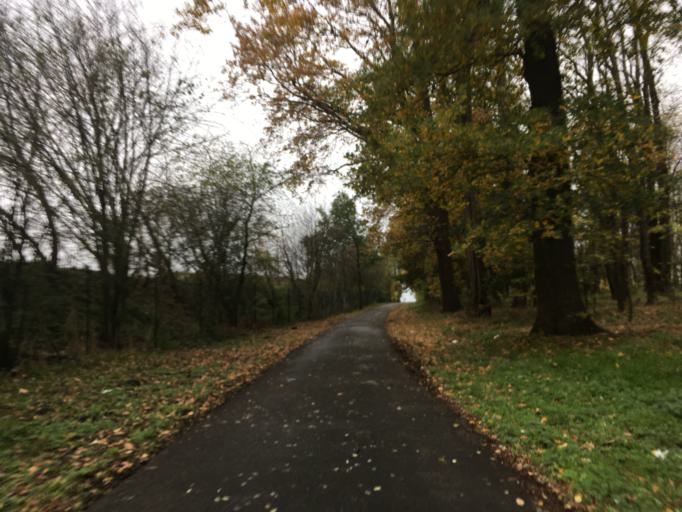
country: DE
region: Brandenburg
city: Frankfurt (Oder)
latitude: 52.3014
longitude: 14.5249
